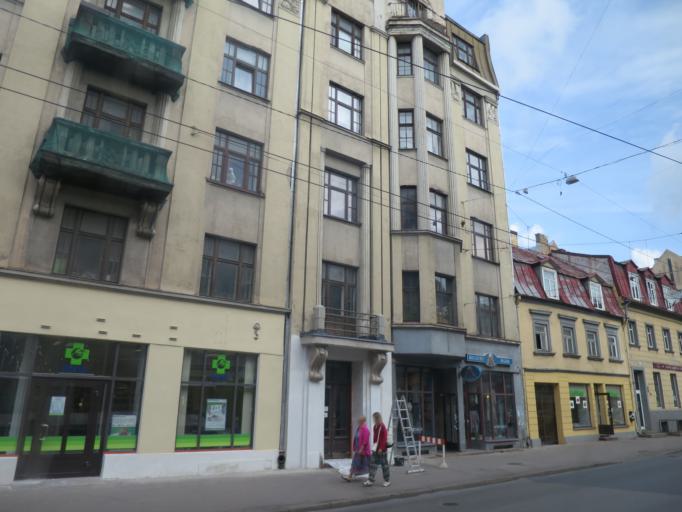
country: LV
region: Riga
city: Riga
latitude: 56.9537
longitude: 24.1317
